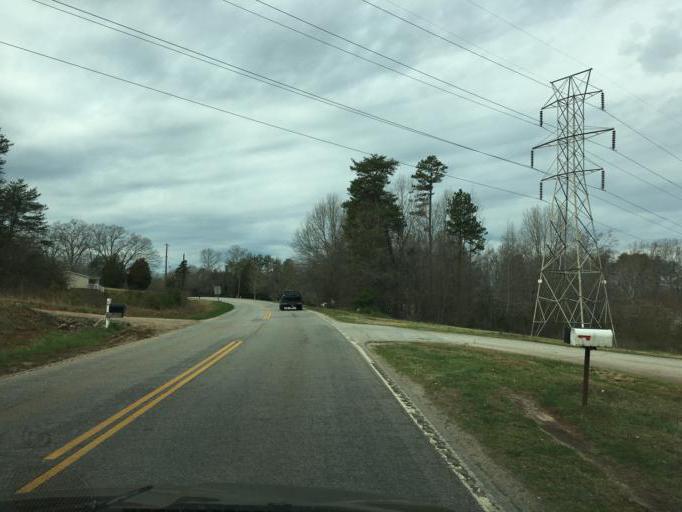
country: US
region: South Carolina
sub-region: Greenville County
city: Golden Grove
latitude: 34.6987
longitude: -82.4156
